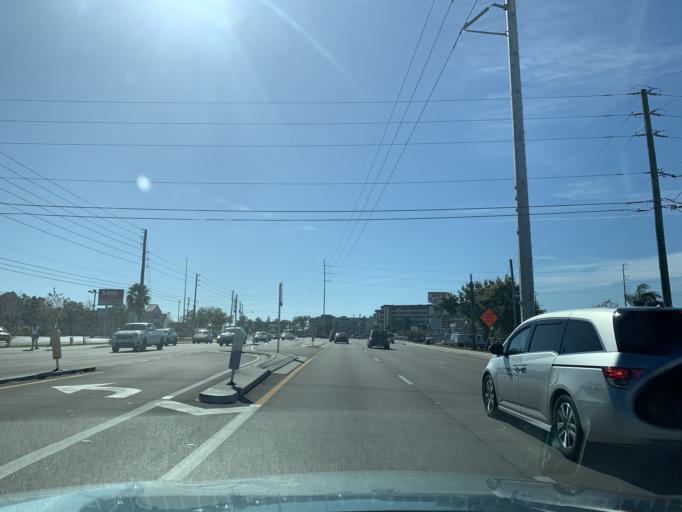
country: US
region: Florida
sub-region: Pinellas County
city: Seminole
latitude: 27.8415
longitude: -82.7625
